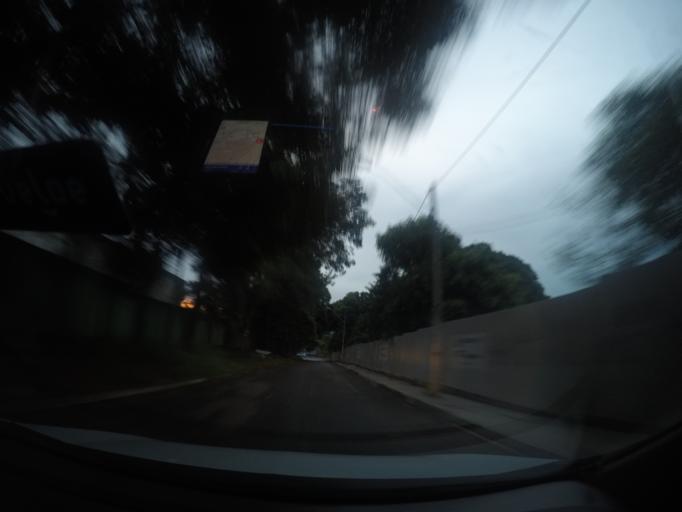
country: BR
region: Goias
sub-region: Goiania
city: Goiania
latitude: -16.6416
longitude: -49.2458
